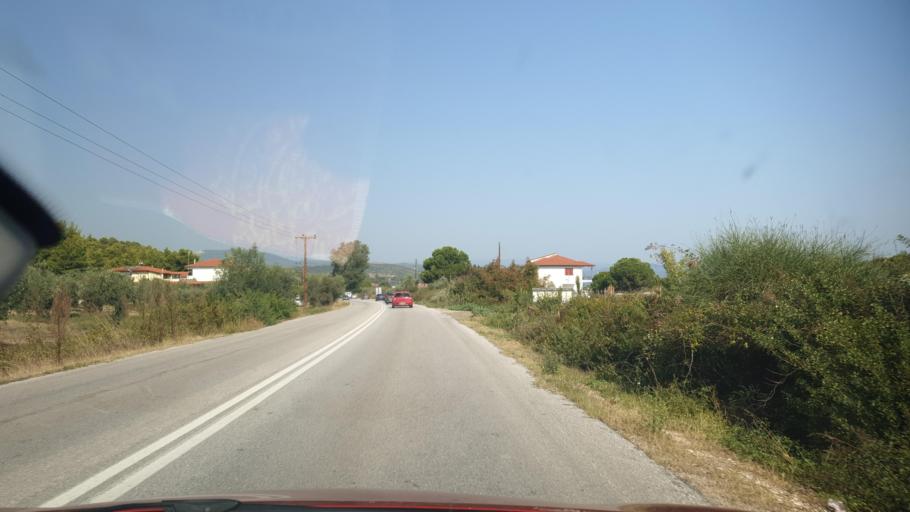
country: GR
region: Central Macedonia
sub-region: Nomos Chalkidikis
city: Agios Nikolaos
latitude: 40.2256
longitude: 23.7436
